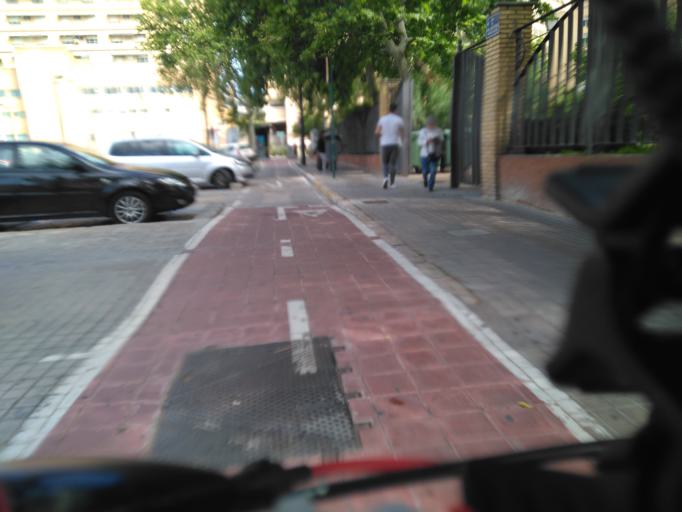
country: ES
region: Valencia
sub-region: Provincia de Valencia
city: Valencia
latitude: 39.4820
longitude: -0.3900
